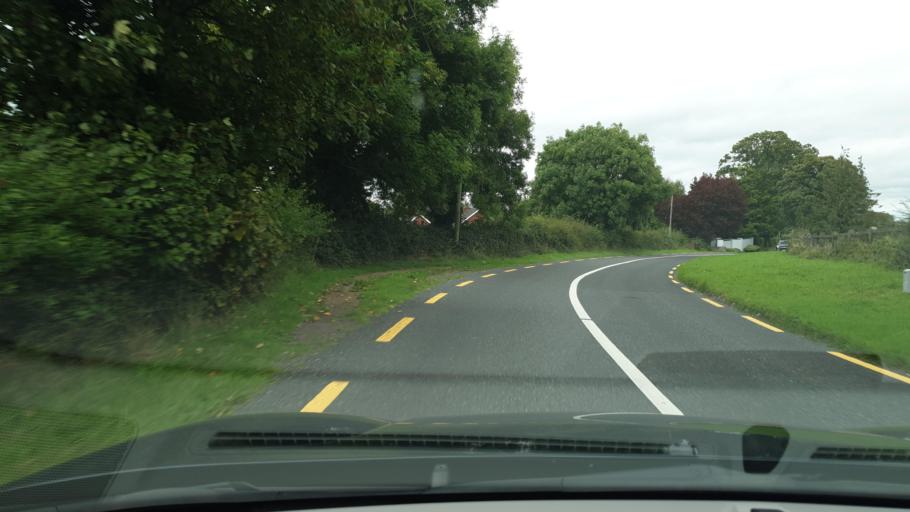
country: IE
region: Leinster
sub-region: Kildare
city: Sallins
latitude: 53.2346
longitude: -6.6942
